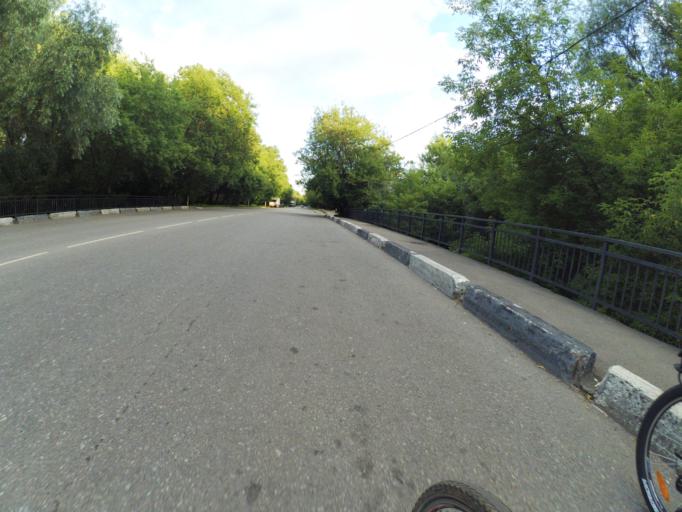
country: RU
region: Moscow
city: Strogino
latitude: 55.8376
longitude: 37.4239
